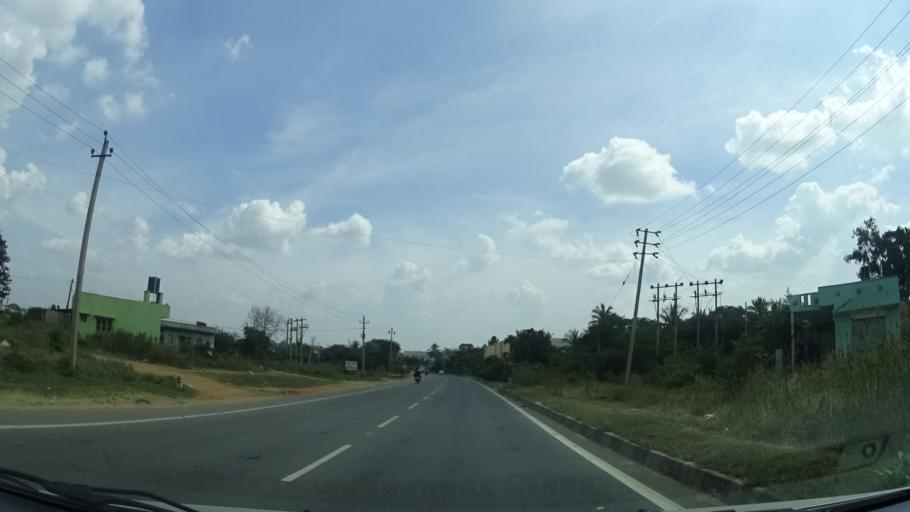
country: IN
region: Karnataka
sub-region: Bangalore Rural
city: Nelamangala
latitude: 13.1487
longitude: 77.3403
